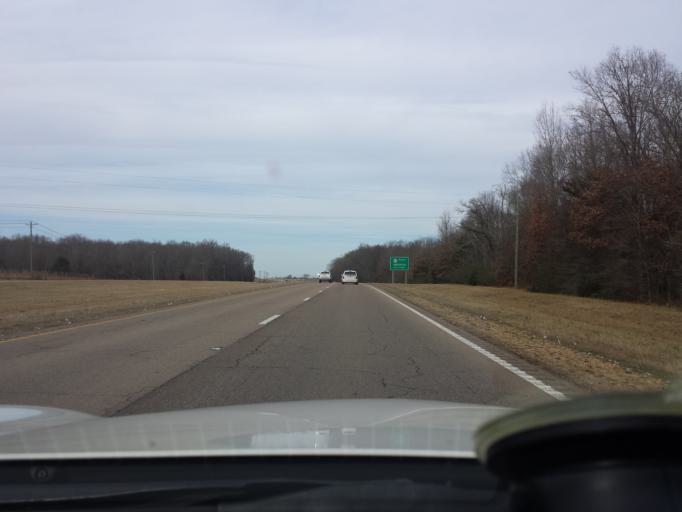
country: US
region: Mississippi
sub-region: Clay County
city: West Point
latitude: 33.7010
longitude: -88.6678
